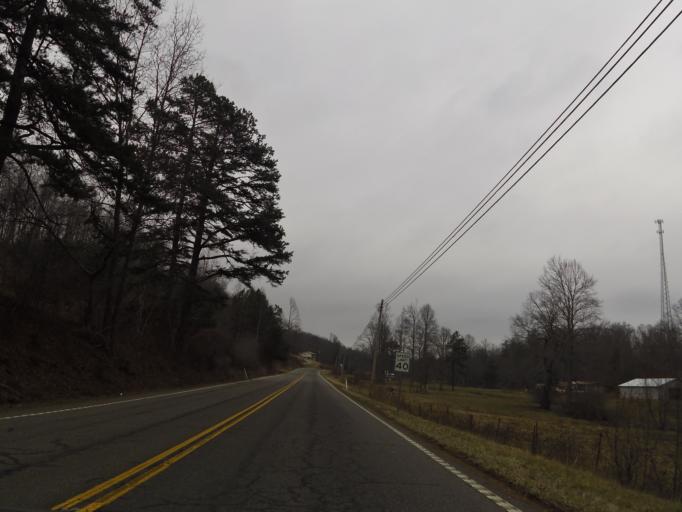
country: US
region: Tennessee
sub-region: Morgan County
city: Wartburg
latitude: 36.2736
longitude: -84.6550
